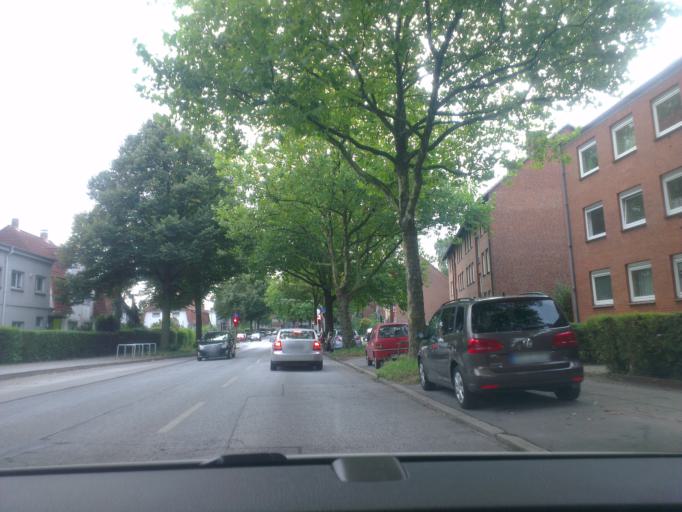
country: DE
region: Hamburg
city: Marienthal
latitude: 53.5900
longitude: 10.0778
